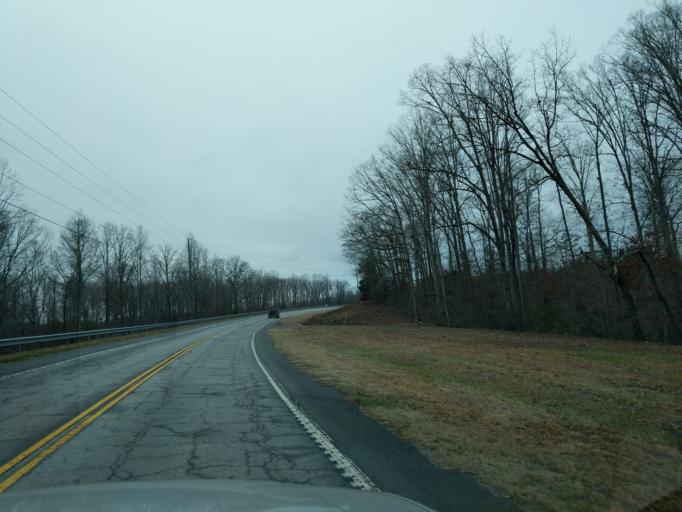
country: US
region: South Carolina
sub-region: Oconee County
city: Walhalla
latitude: 34.8365
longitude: -83.0383
